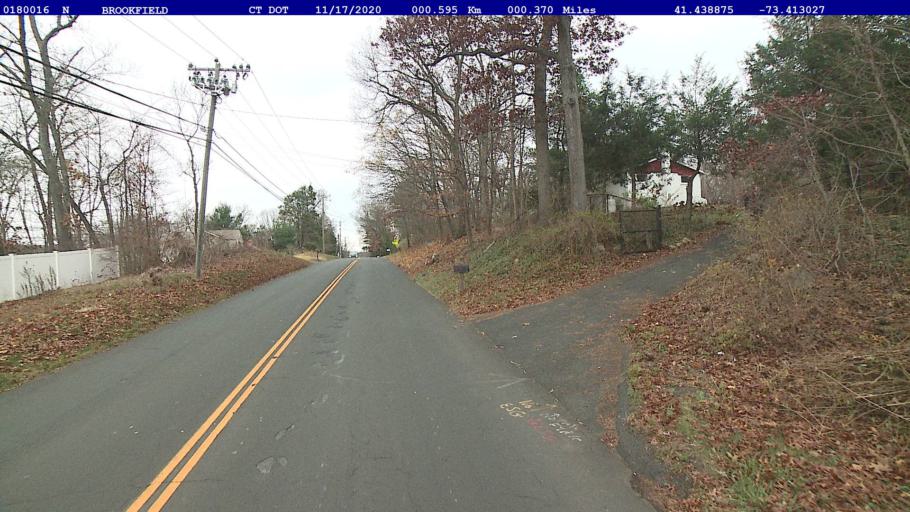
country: US
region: Connecticut
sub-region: Fairfield County
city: Danbury
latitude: 41.4389
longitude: -73.4130
